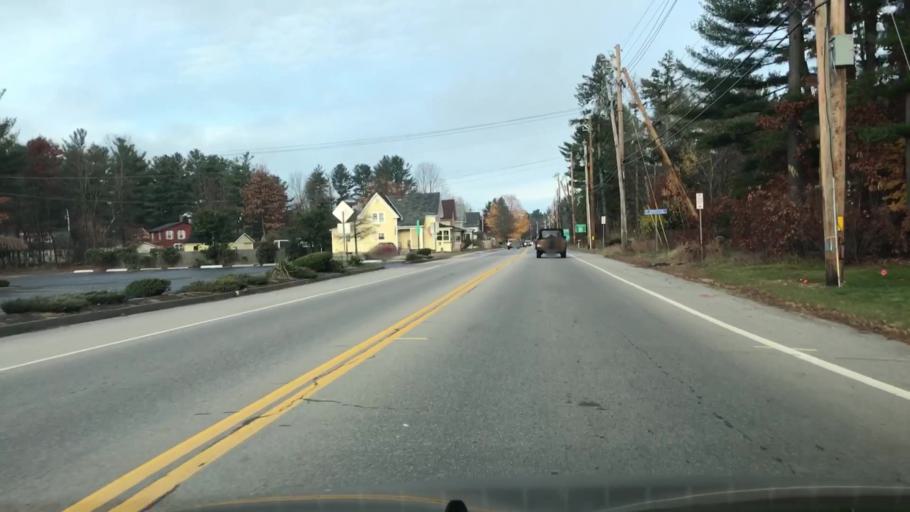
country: US
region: New Hampshire
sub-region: Cheshire County
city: Keene
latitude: 42.9108
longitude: -72.2630
